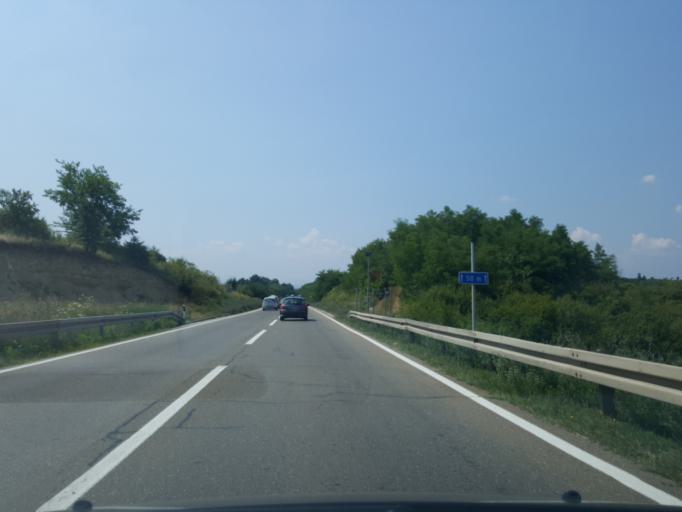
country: RS
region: Central Serbia
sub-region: Belgrade
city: Sopot
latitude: 44.5317
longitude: 20.6562
